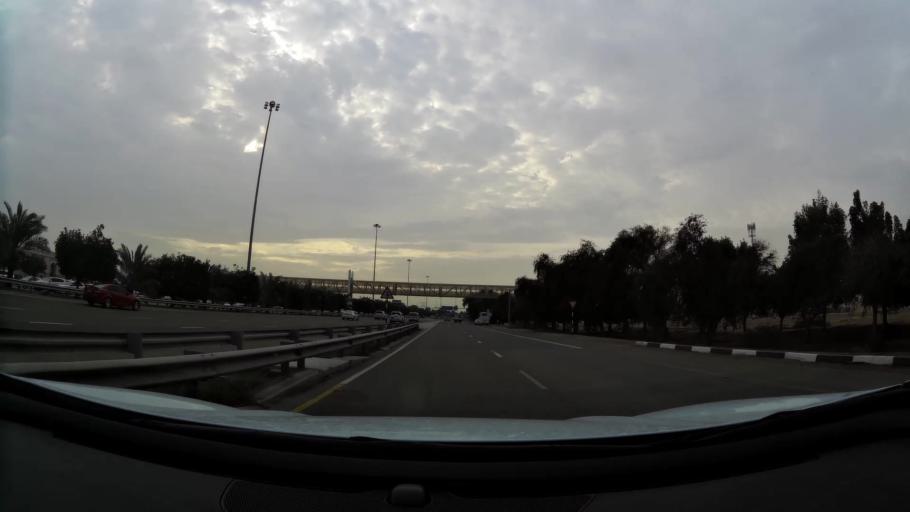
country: AE
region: Abu Dhabi
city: Abu Dhabi
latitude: 24.3646
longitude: 54.5612
